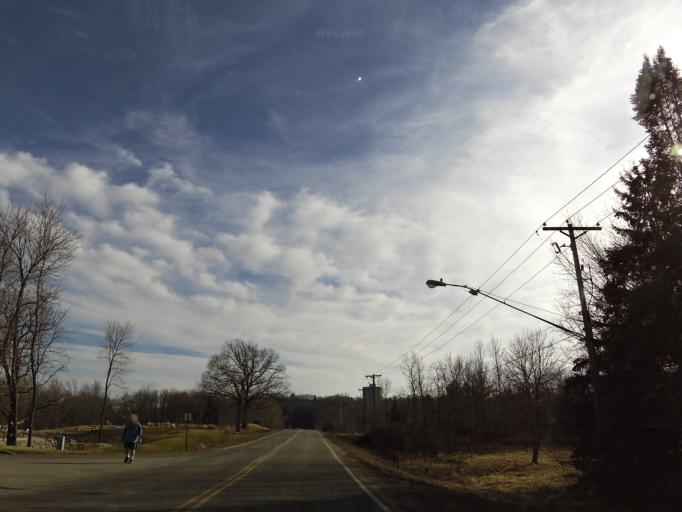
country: US
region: Minnesota
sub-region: Rice County
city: Northfield
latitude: 44.4698
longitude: -93.1808
